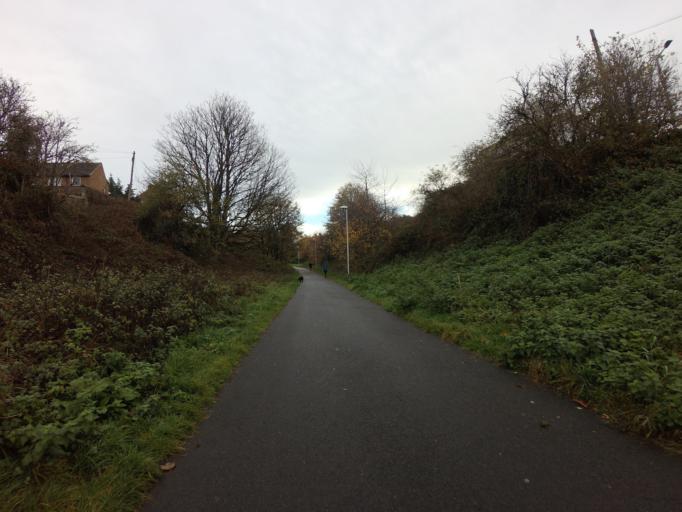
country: GB
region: Scotland
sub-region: West Lothian
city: Seafield
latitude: 55.9666
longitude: -3.1507
